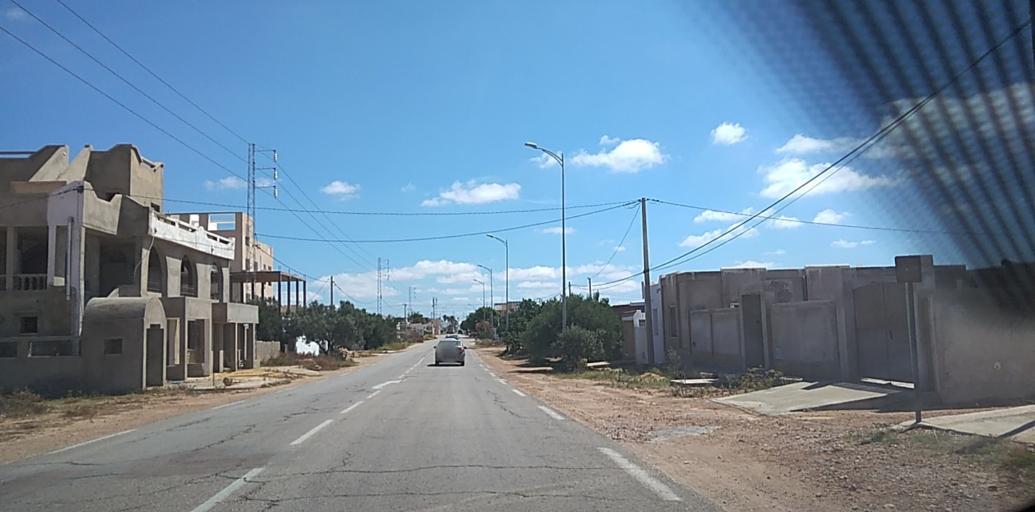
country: TN
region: Safaqis
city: Al Qarmadah
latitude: 34.6699
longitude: 11.1356
